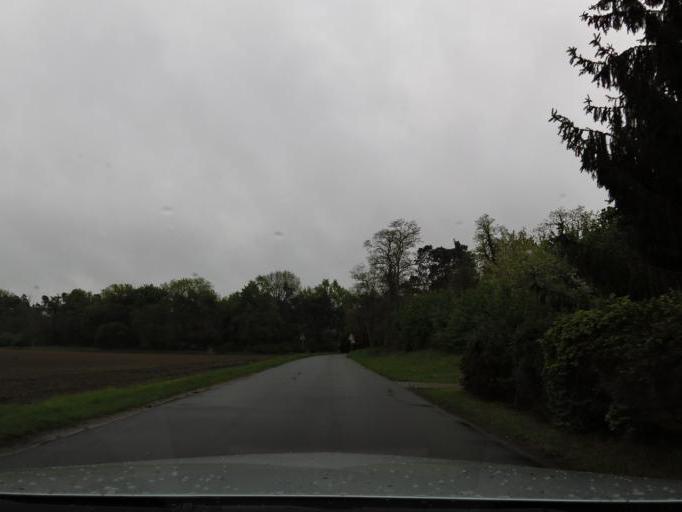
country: DE
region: Hesse
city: Weiterstadt
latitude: 49.8820
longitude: 8.5873
